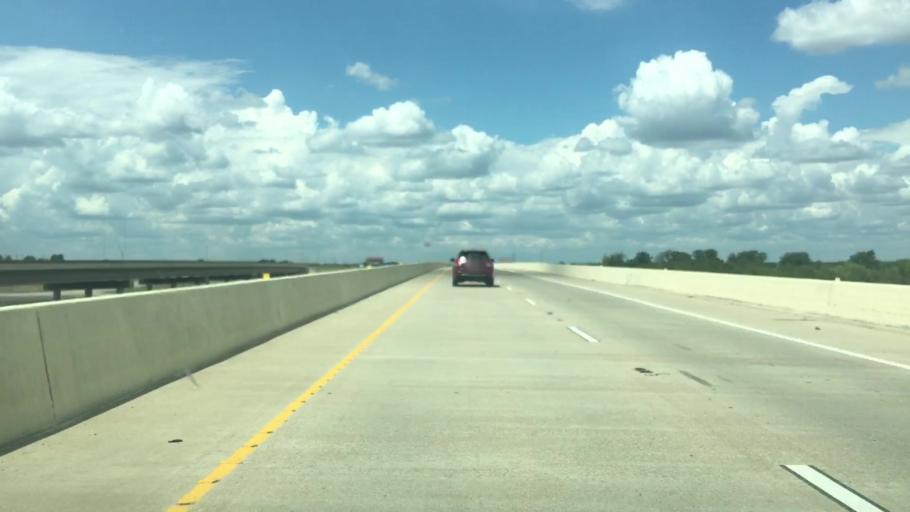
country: US
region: Texas
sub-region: Williamson County
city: Georgetown
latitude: 30.6208
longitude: -97.6138
